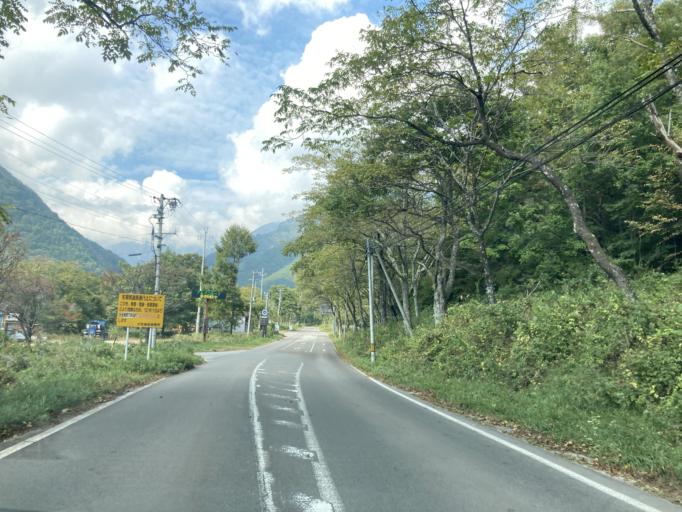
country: JP
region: Nagano
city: Omachi
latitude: 36.5347
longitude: 137.7908
